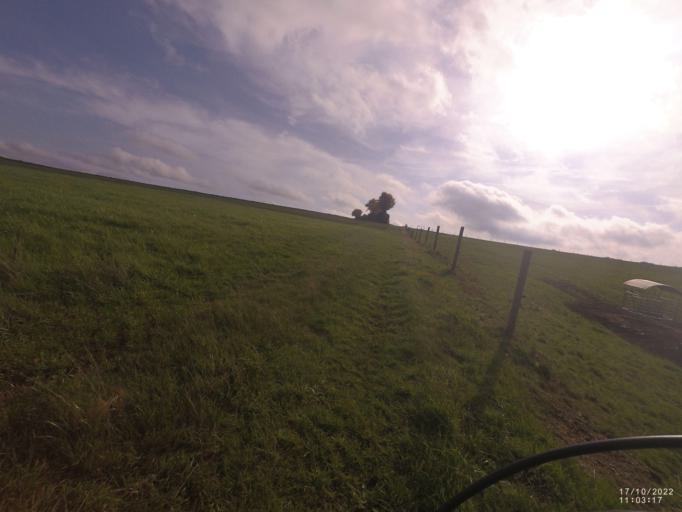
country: DE
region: Rheinland-Pfalz
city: Steiningen
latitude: 50.1851
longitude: 6.9236
